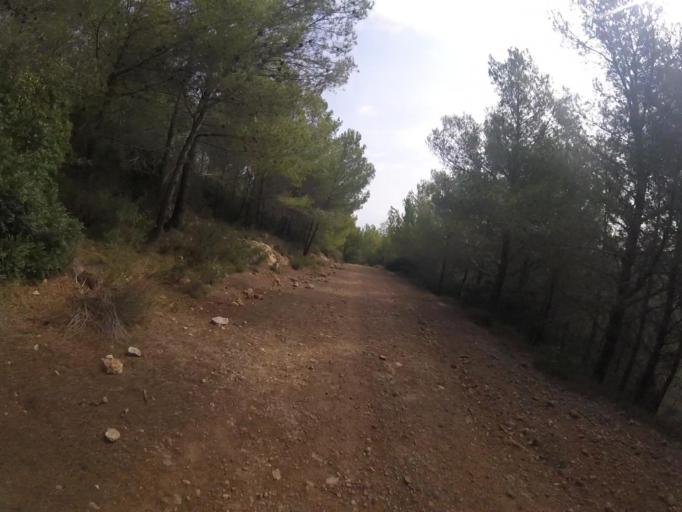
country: ES
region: Valencia
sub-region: Provincia de Castello
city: Benicassim
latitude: 40.0868
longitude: 0.0475
